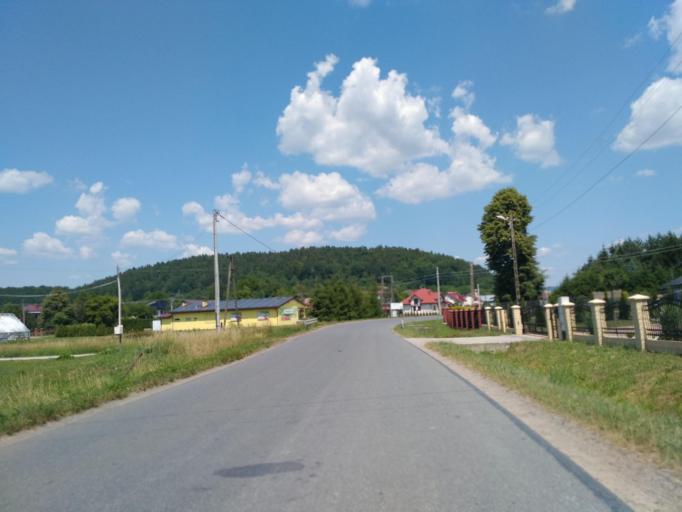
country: PL
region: Subcarpathian Voivodeship
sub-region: Powiat sanocki
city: Niebieszczany
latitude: 49.5445
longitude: 22.1349
